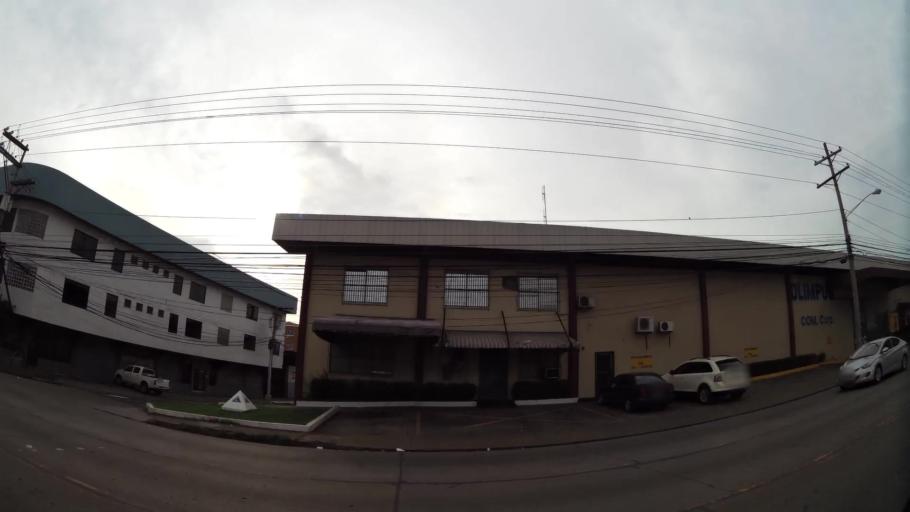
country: PA
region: Panama
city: Panama
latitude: 9.0021
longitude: -79.5200
